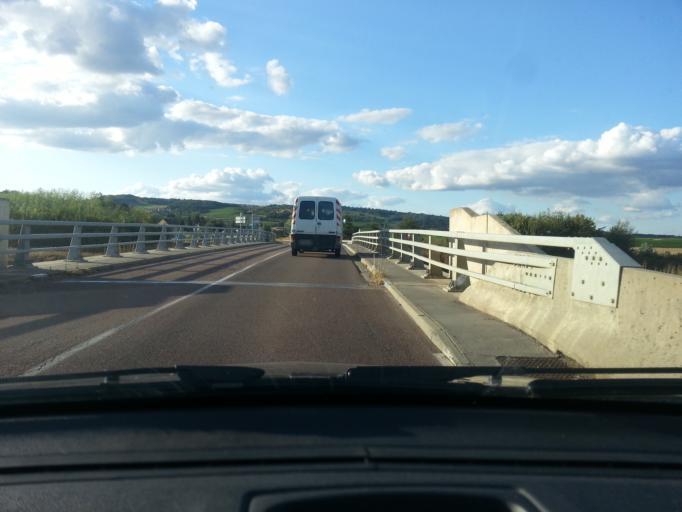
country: FR
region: Bourgogne
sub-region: Departement de Saone-et-Loire
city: Givry
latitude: 46.7571
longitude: 4.7191
